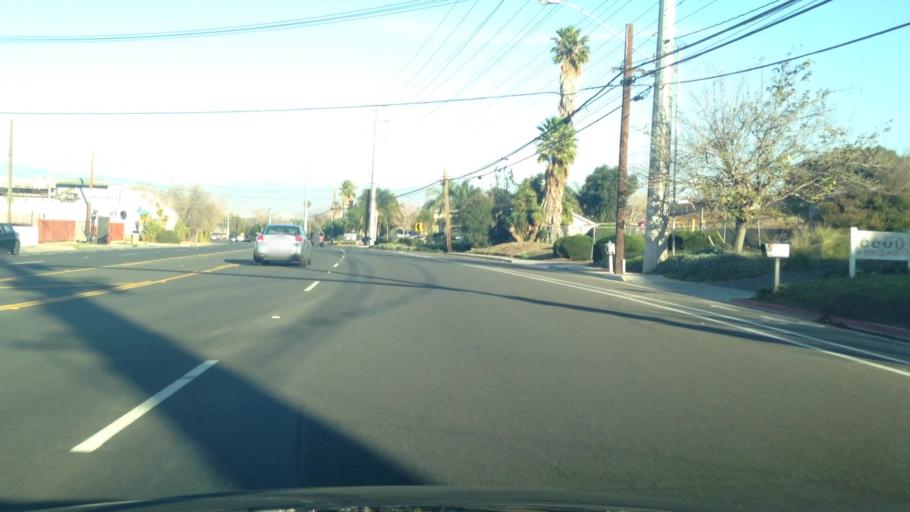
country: US
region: California
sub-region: Riverside County
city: Pedley
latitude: 33.9608
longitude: -117.4405
